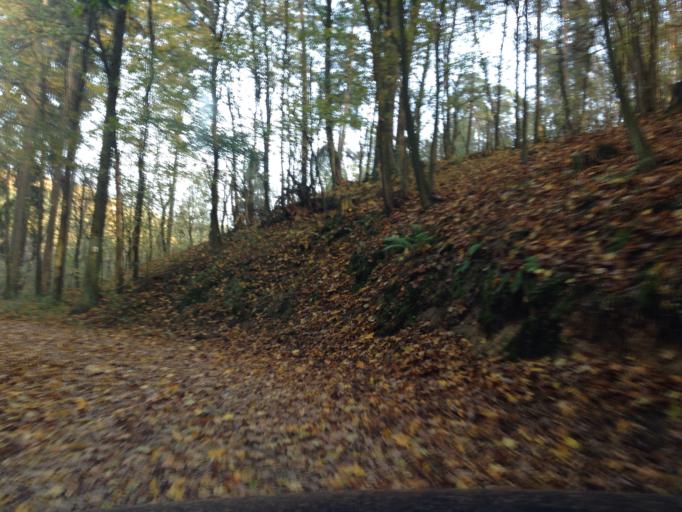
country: PL
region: Kujawsko-Pomorskie
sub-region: Powiat brodnicki
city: Gorzno
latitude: 53.2602
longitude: 19.7201
